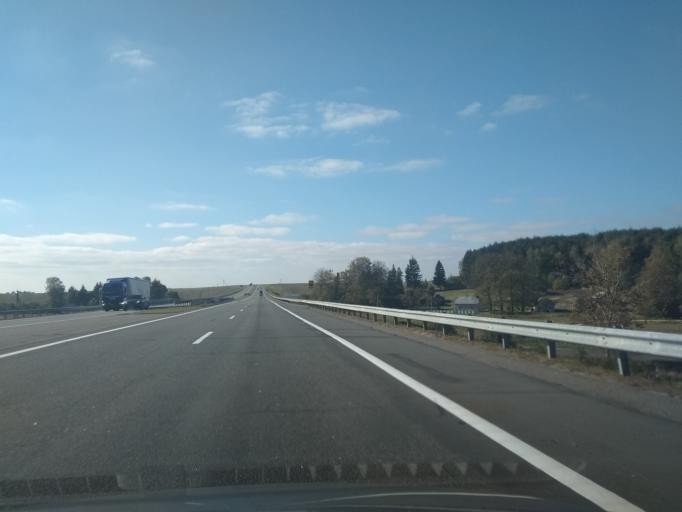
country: BY
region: Minsk
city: Snow
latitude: 53.2961
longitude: 26.3608
